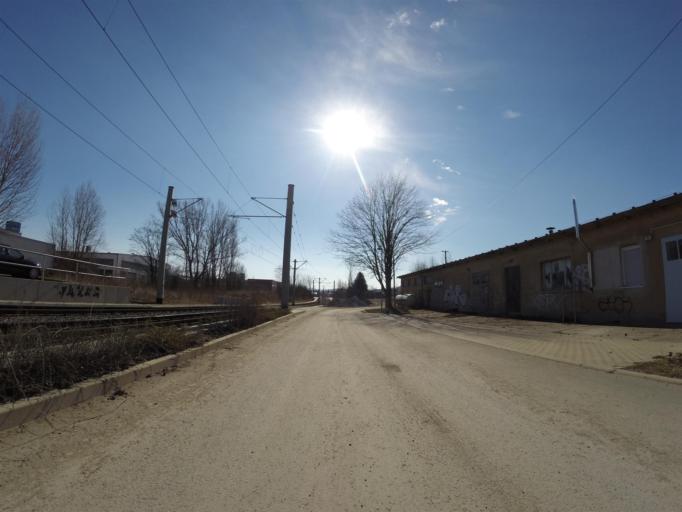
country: DE
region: Thuringia
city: Sulza
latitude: 50.8884
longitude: 11.5941
